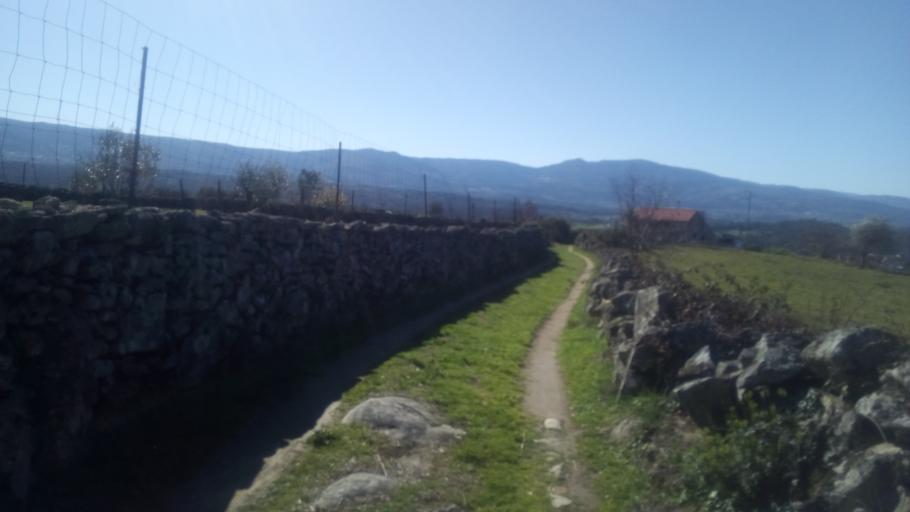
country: PT
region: Guarda
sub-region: Fornos de Algodres
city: Fornos de Algodres
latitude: 40.6033
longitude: -7.5069
